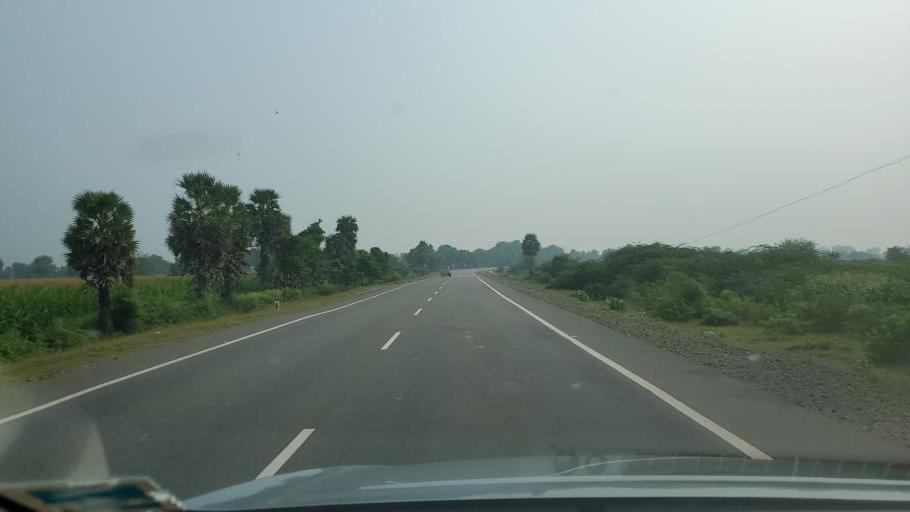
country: IN
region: Tamil Nadu
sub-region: Perambalur
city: Perambalur
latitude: 11.2412
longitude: 79.0044
